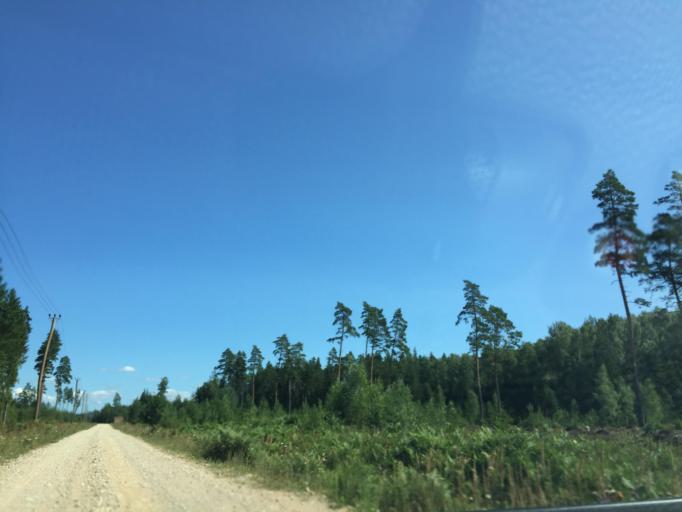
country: LV
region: Talsu Rajons
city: Stende
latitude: 57.1733
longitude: 22.3050
